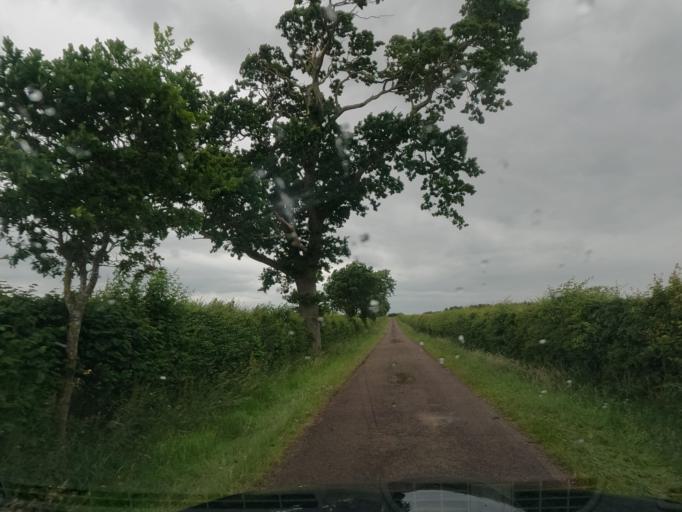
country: GB
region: England
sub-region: Northumberland
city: Ford
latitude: 55.6922
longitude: -2.1541
